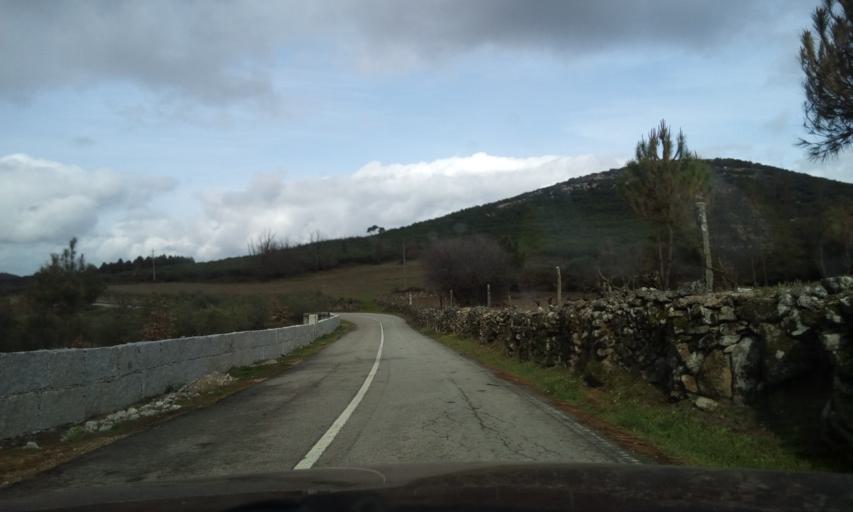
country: PT
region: Guarda
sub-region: Fornos de Algodres
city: Fornos de Algodres
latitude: 40.6578
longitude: -7.5860
